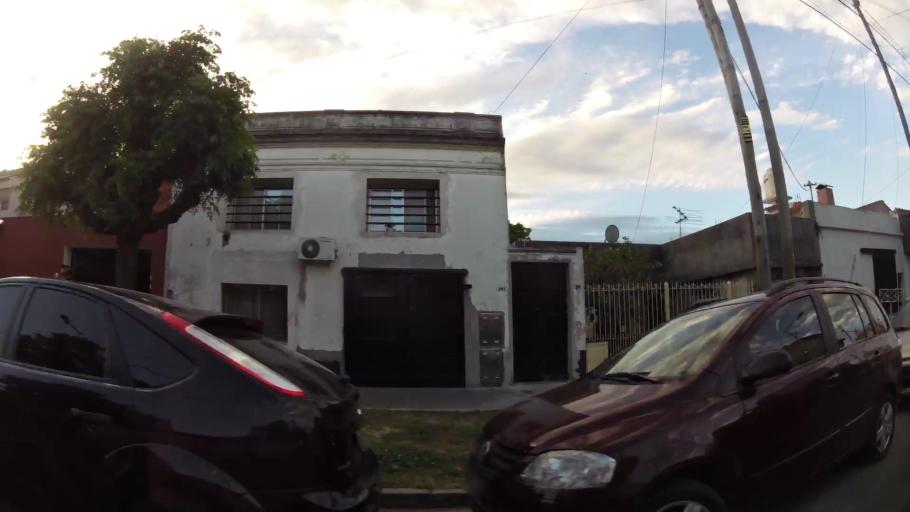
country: AR
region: Buenos Aires
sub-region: Partido de Avellaneda
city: Avellaneda
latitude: -34.6942
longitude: -58.3445
